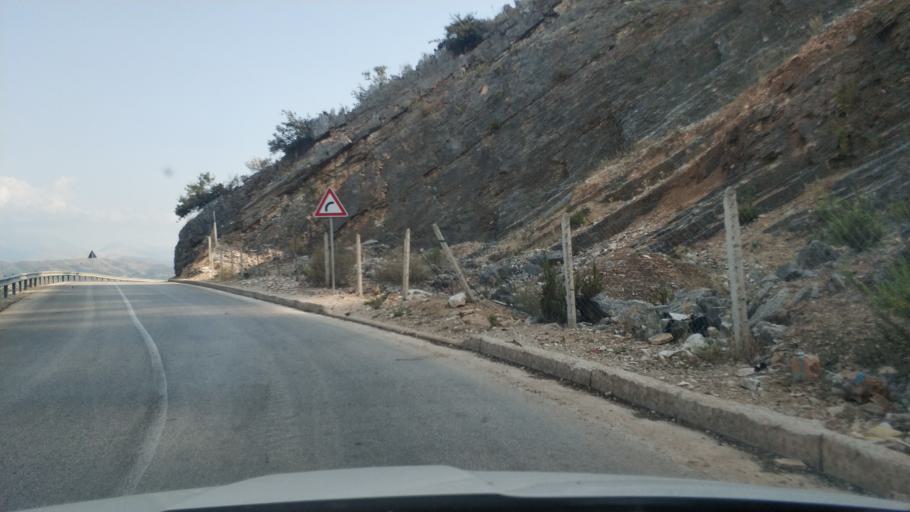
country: AL
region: Vlore
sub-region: Rrethi i Sarandes
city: Sarande
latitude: 39.8665
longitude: 20.0314
